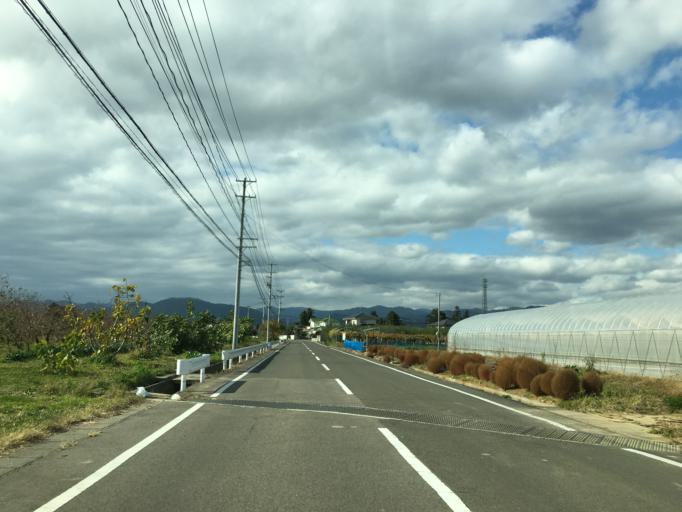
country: JP
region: Fukushima
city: Fukushima-shi
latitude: 37.8039
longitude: 140.4694
